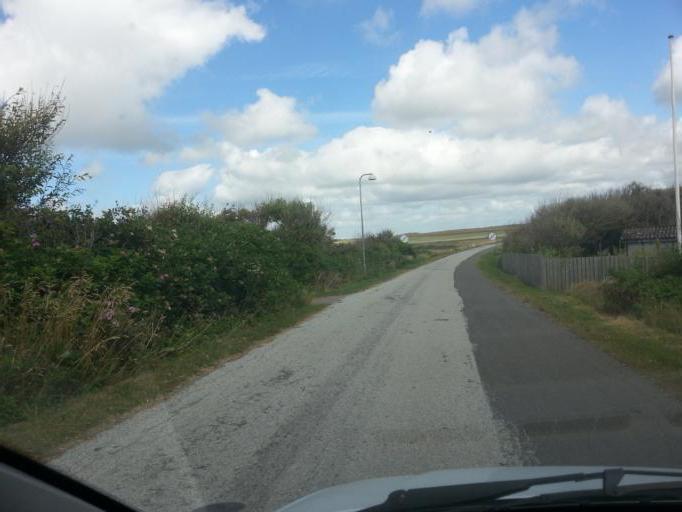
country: DK
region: Central Jutland
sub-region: Lemvig Kommune
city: Harboore
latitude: 56.5257
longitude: 8.1238
